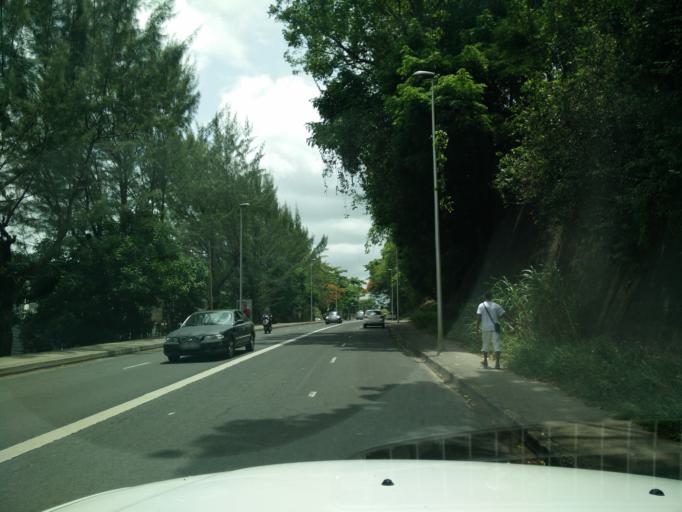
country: GP
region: Guadeloupe
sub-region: Guadeloupe
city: Pointe-a-Pitre
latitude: 16.2474
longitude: -61.5352
